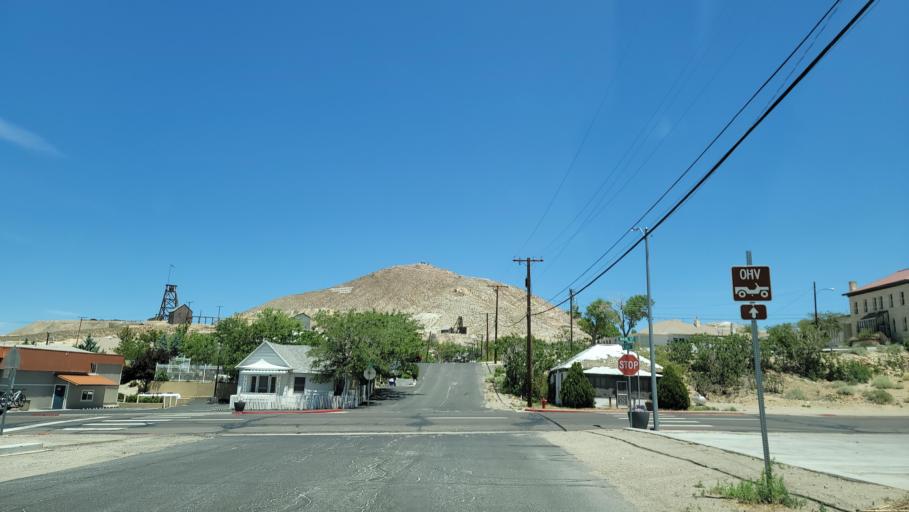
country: US
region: Nevada
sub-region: Nye County
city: Tonopah
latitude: 38.0652
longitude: -117.2283
